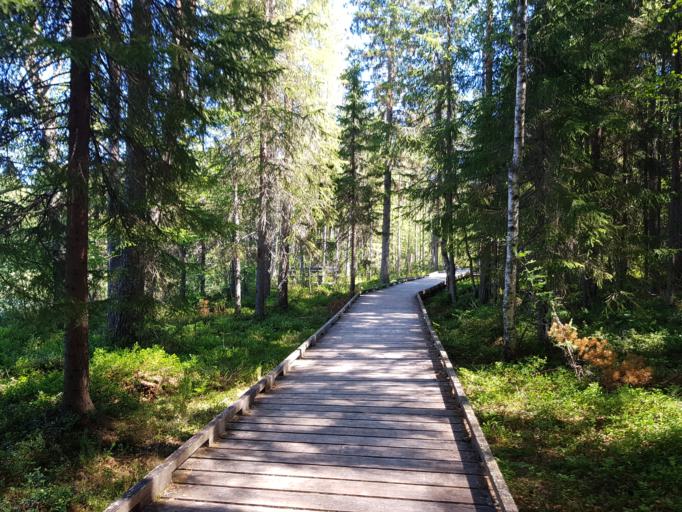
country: FI
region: Kainuu
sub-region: Kehys-Kainuu
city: Kuhmo
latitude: 64.1934
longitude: 29.5927
